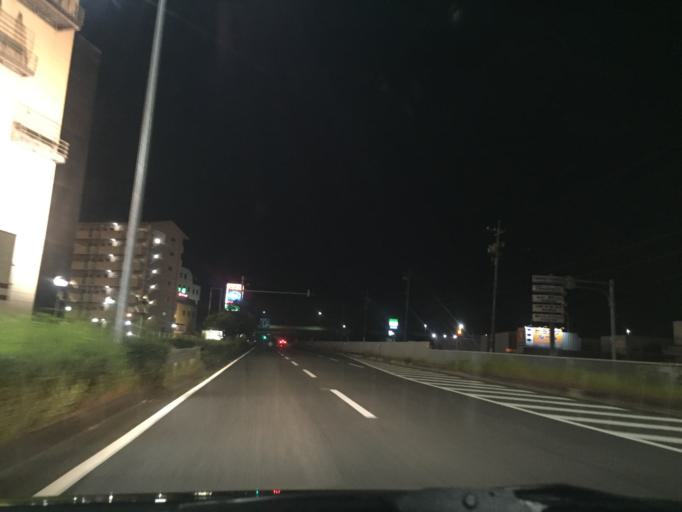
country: JP
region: Aichi
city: Handa
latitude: 34.8854
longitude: 136.9409
